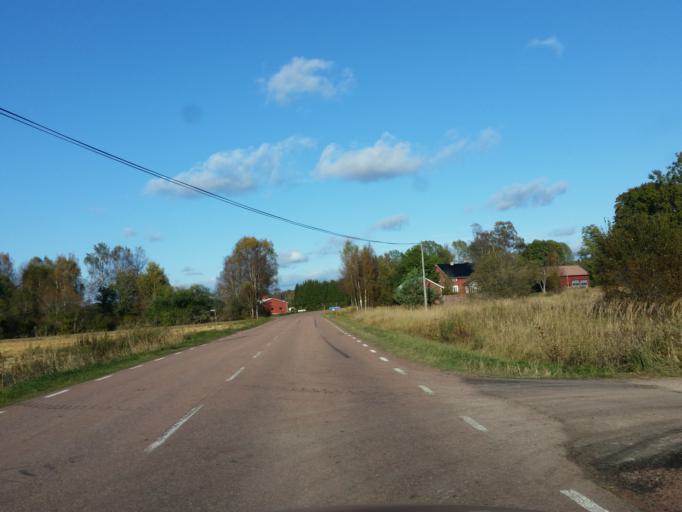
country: AX
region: Alands landsbygd
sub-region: Jomala
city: Jomala
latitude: 60.1524
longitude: 19.8682
